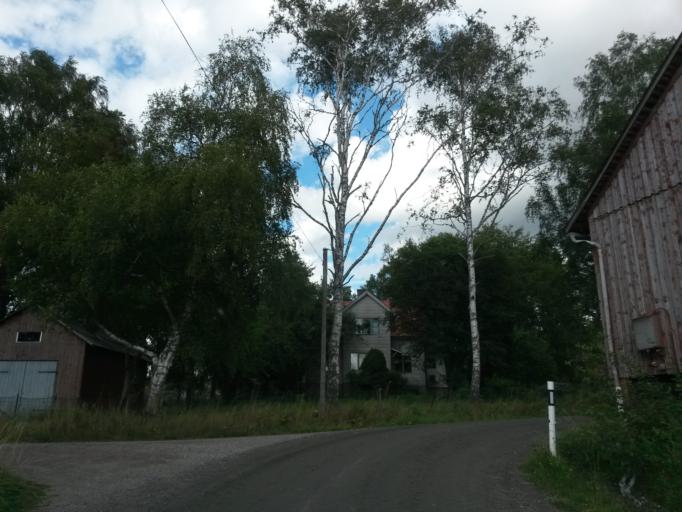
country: SE
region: Vaestra Goetaland
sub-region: Vargarda Kommun
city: Jonstorp
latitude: 57.9955
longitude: 12.6356
